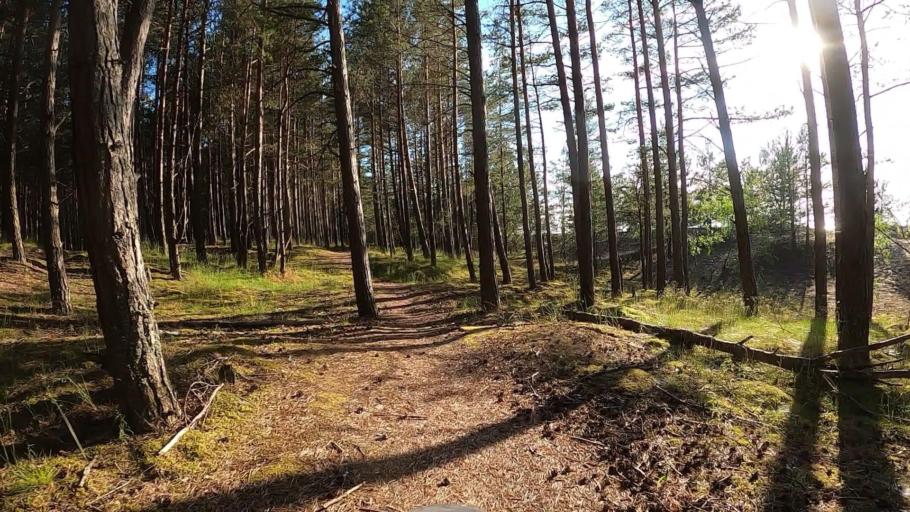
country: LV
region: Carnikava
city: Carnikava
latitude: 57.1237
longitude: 24.2112
